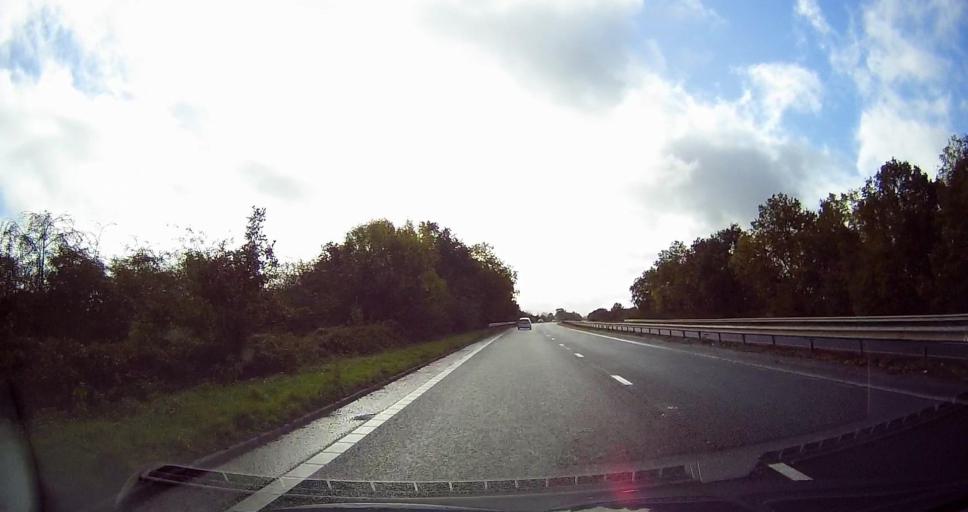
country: GB
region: England
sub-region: Warwickshire
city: Curdworth
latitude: 52.5610
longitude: -1.7703
